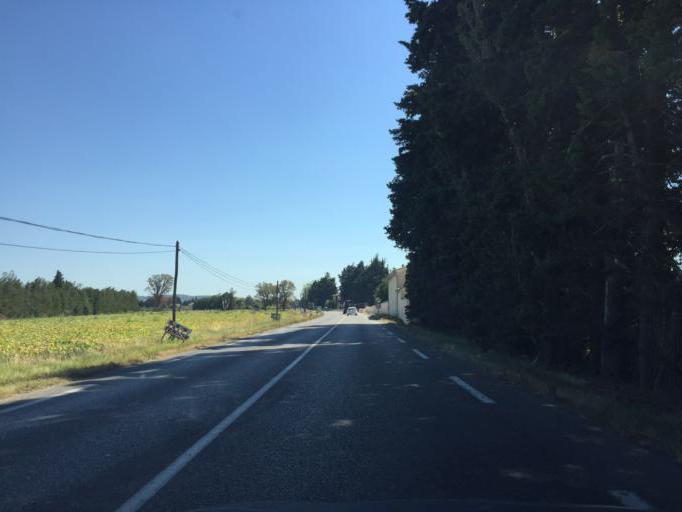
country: FR
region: Provence-Alpes-Cote d'Azur
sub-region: Departement du Vaucluse
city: L'Isle-sur-la-Sorgue
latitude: 43.8741
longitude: 5.0603
